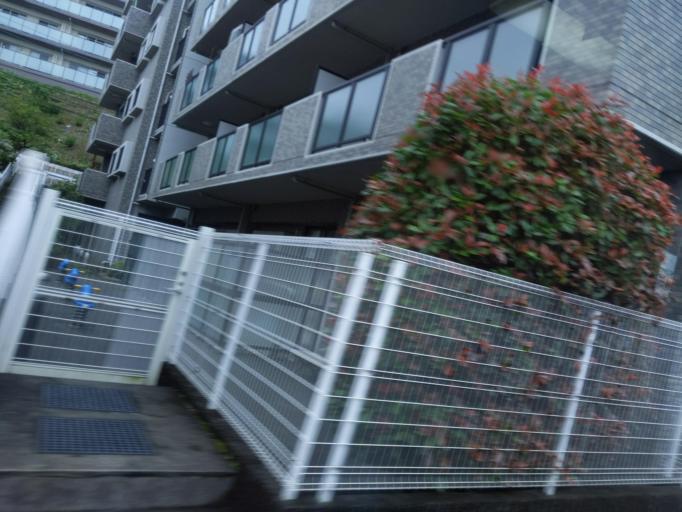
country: JP
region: Tokyo
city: Chofugaoka
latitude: 35.6094
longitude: 139.5830
